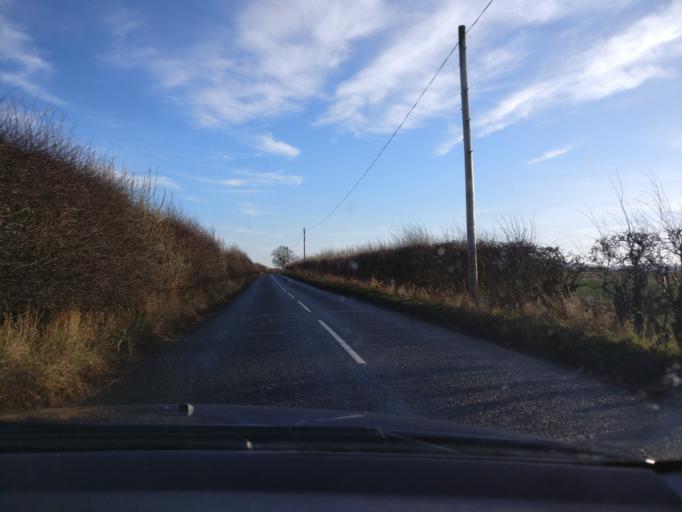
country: GB
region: Scotland
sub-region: The Scottish Borders
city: Kelso
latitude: 55.5337
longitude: -2.4425
